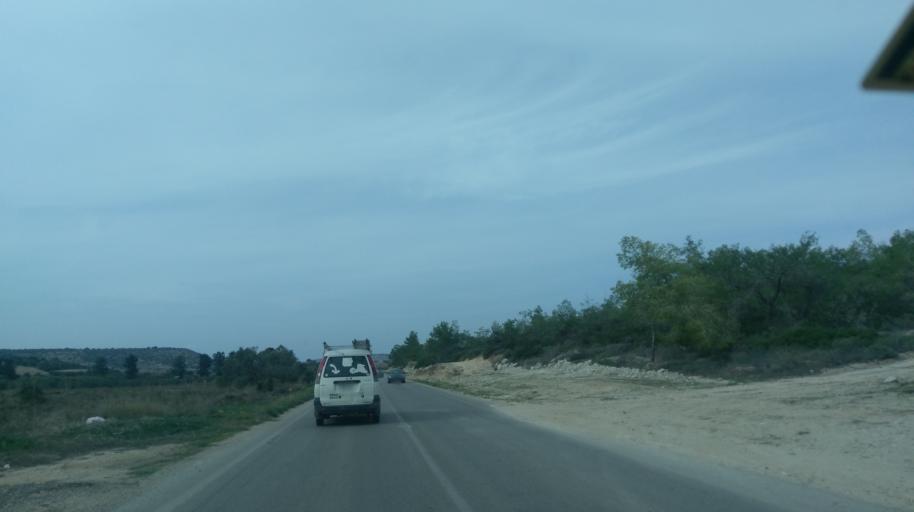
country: CY
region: Ammochostos
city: Leonarisso
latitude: 35.4499
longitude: 34.1304
